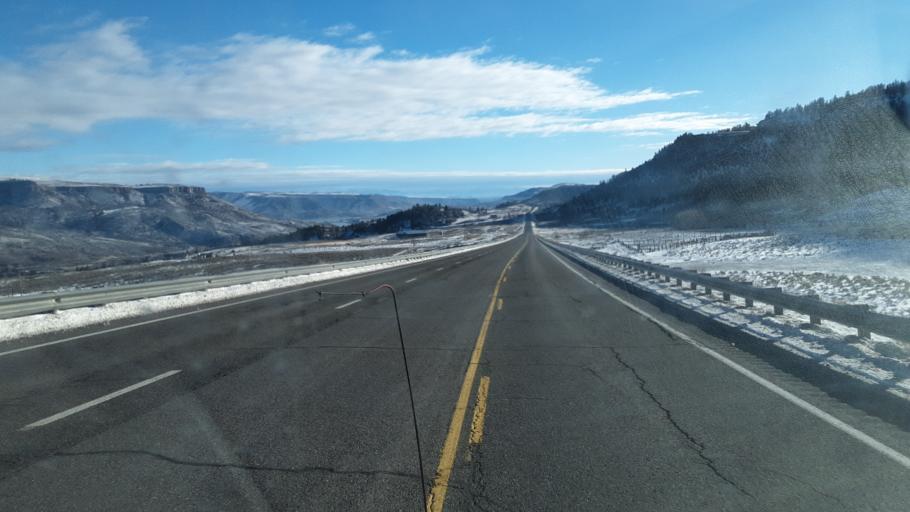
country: US
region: Colorado
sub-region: Hinsdale County
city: Lake City
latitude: 38.4372
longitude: -107.3950
